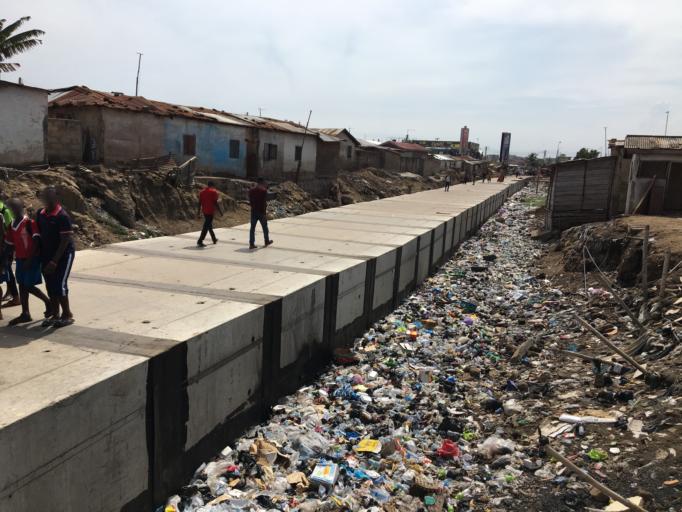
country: GH
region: Greater Accra
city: Accra
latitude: 5.5884
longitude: -0.1947
